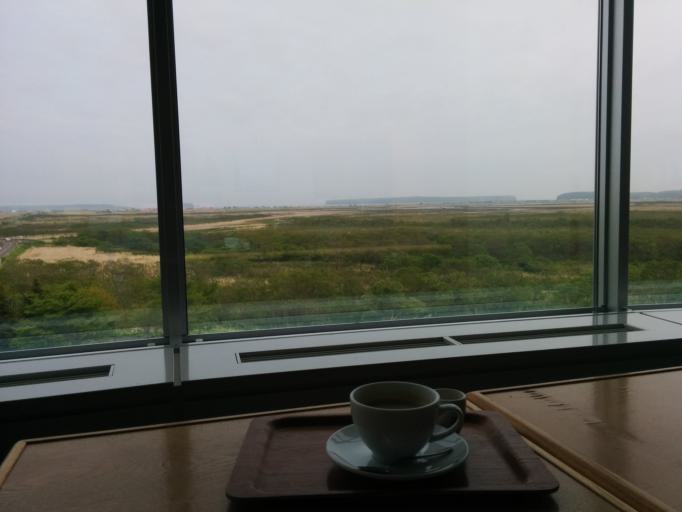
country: JP
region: Hokkaido
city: Nemuro
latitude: 43.0864
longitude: 145.0601
